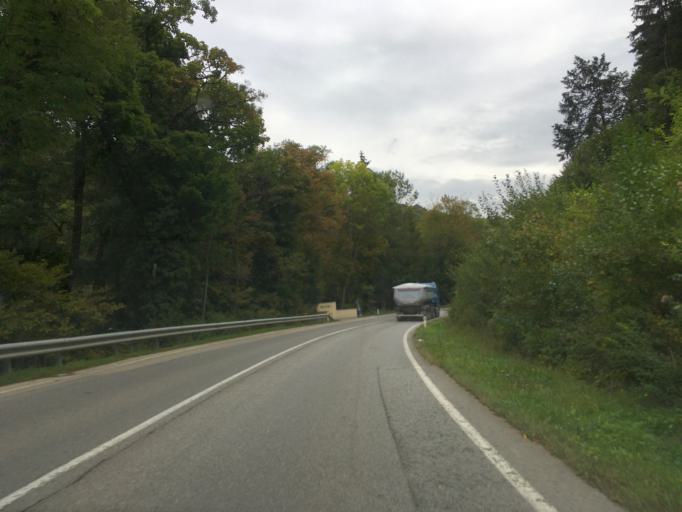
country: AT
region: Lower Austria
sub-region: Politischer Bezirk Modling
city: Gaaden
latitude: 48.0718
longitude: 16.2197
